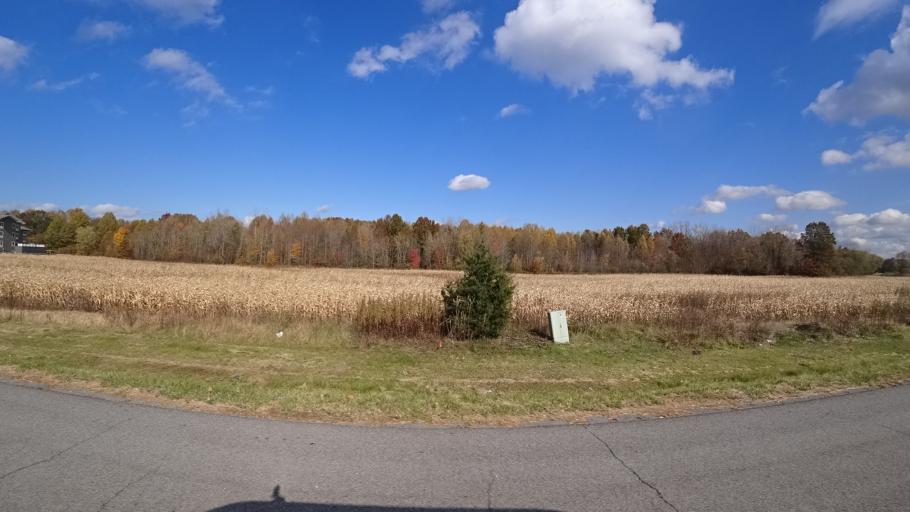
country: US
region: Indiana
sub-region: LaPorte County
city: Trail Creek
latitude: 41.6995
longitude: -86.8325
